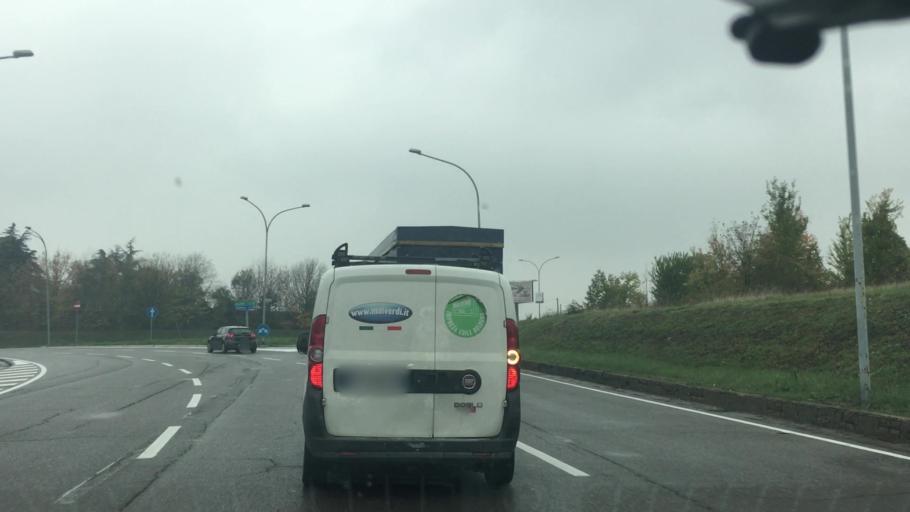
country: IT
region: Emilia-Romagna
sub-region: Provincia di Bologna
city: Casalecchio di Reno
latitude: 44.5113
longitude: 11.2752
